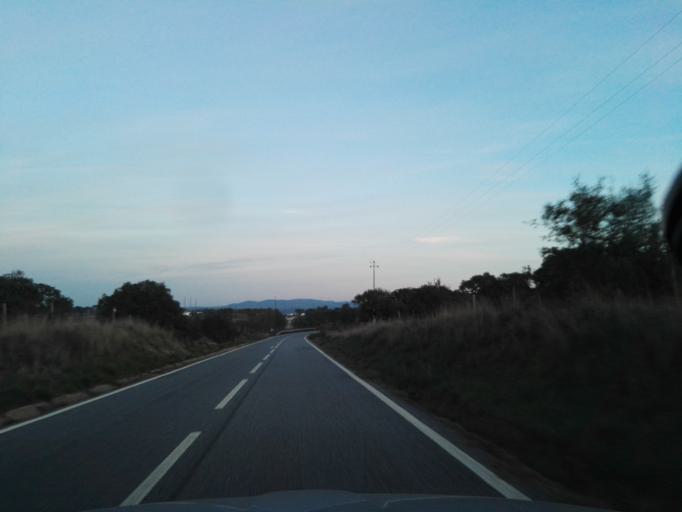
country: PT
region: Evora
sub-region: Montemor-O-Novo
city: Montemor-o-Novo
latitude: 38.7679
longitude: -8.1353
